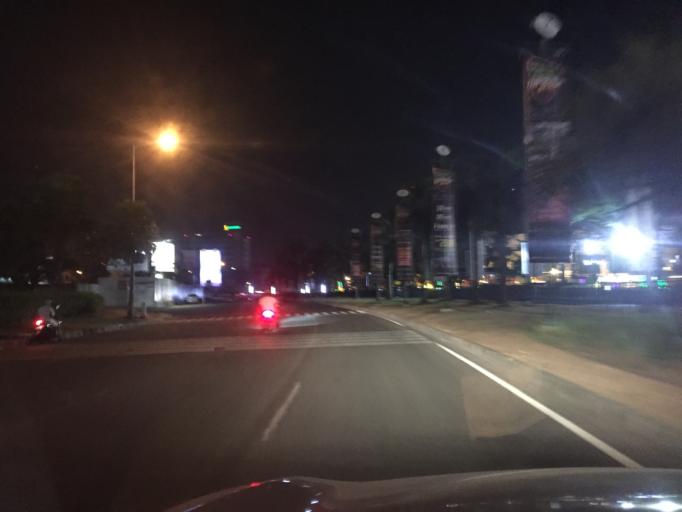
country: ID
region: Banten
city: Tangerang
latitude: -6.2408
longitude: 106.6298
